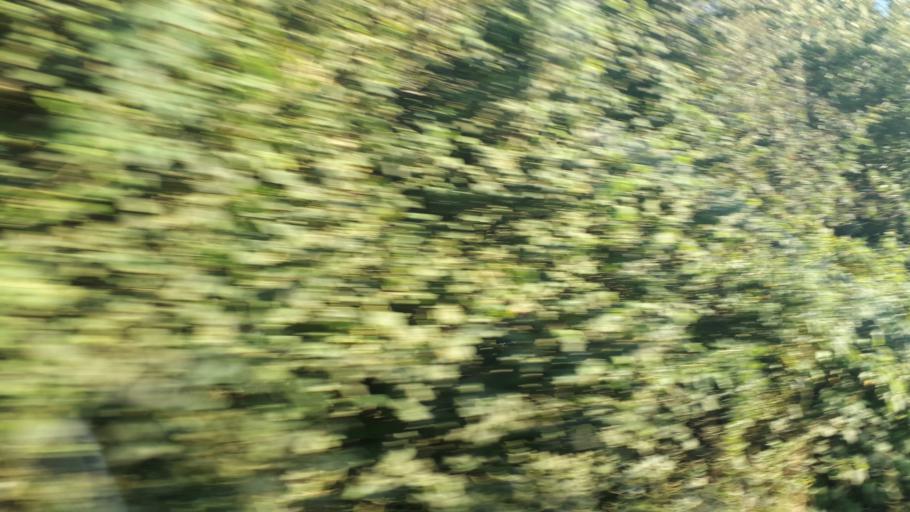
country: IE
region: Leinster
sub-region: Lu
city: Carlingford
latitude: 54.0265
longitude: -6.1360
